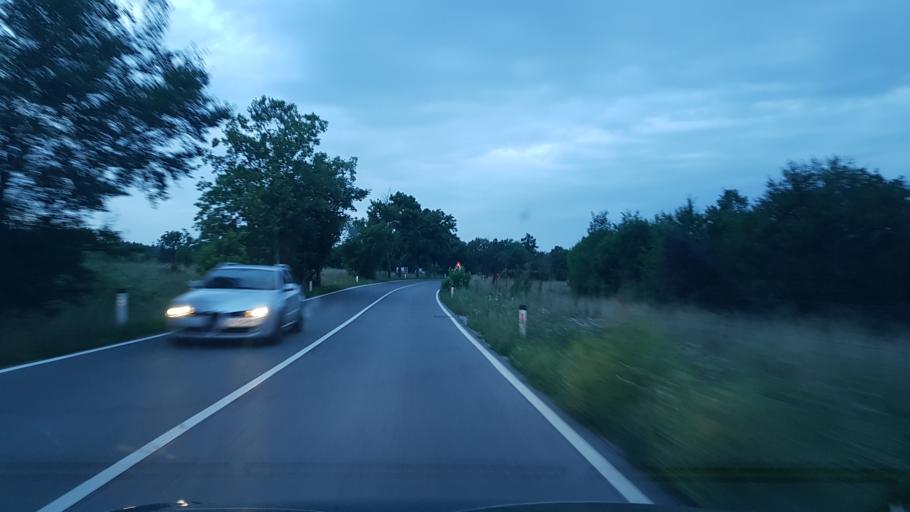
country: SI
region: Divaca
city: Divaca
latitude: 45.6794
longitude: 13.9679
